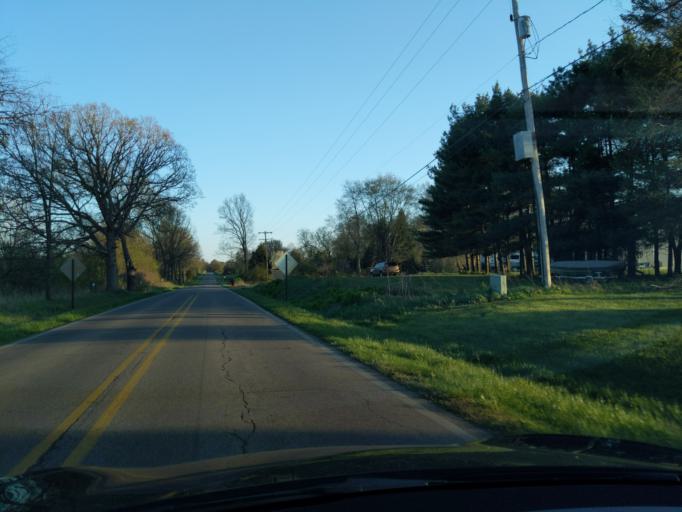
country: US
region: Michigan
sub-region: Jackson County
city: Jackson
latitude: 42.2744
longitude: -84.4832
